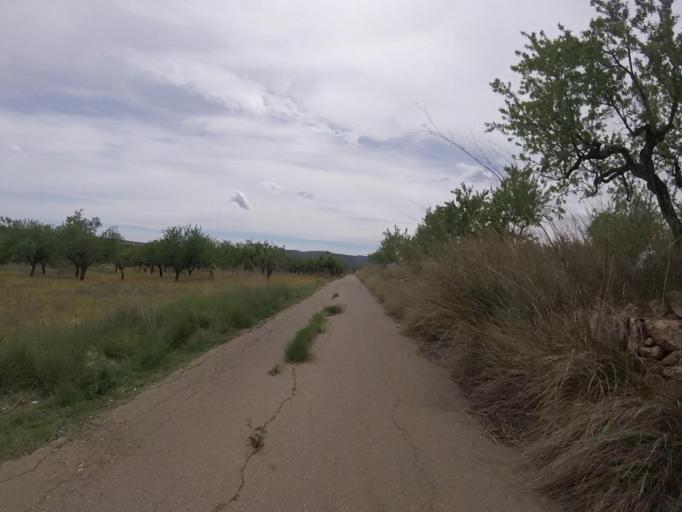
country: ES
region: Valencia
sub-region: Provincia de Castello
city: Benlloch
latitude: 40.1767
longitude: -0.0060
